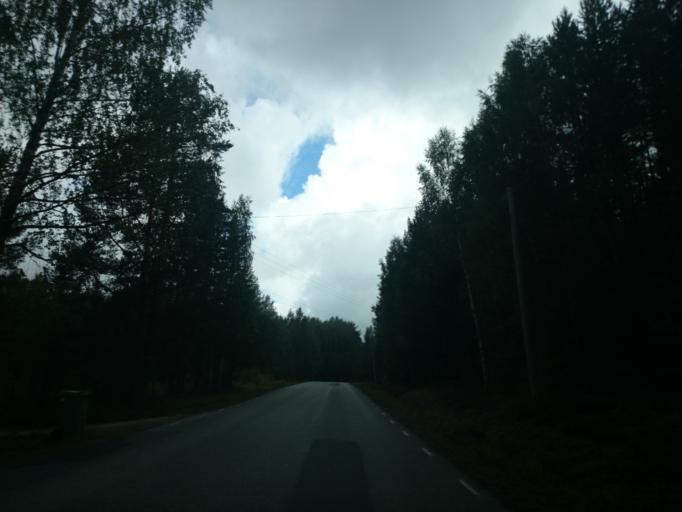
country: SE
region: Vaesternorrland
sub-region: Sundsvalls Kommun
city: Vi
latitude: 62.3026
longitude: 17.2630
